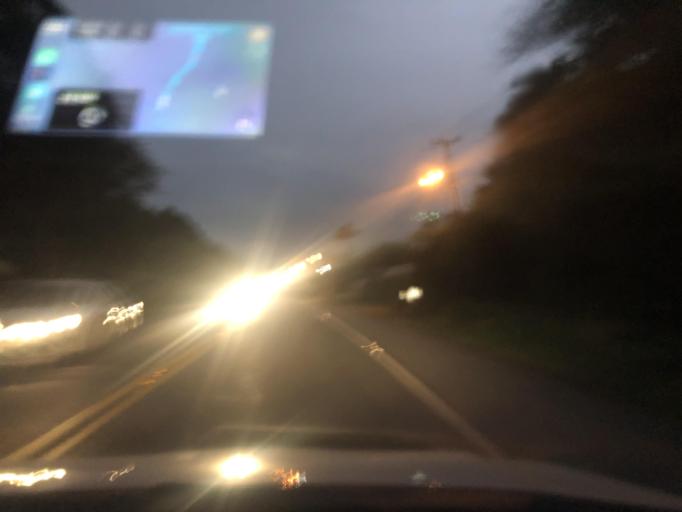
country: BR
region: Santa Catarina
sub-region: Guaramirim
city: Guaramirim
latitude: -26.5926
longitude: -48.9909
